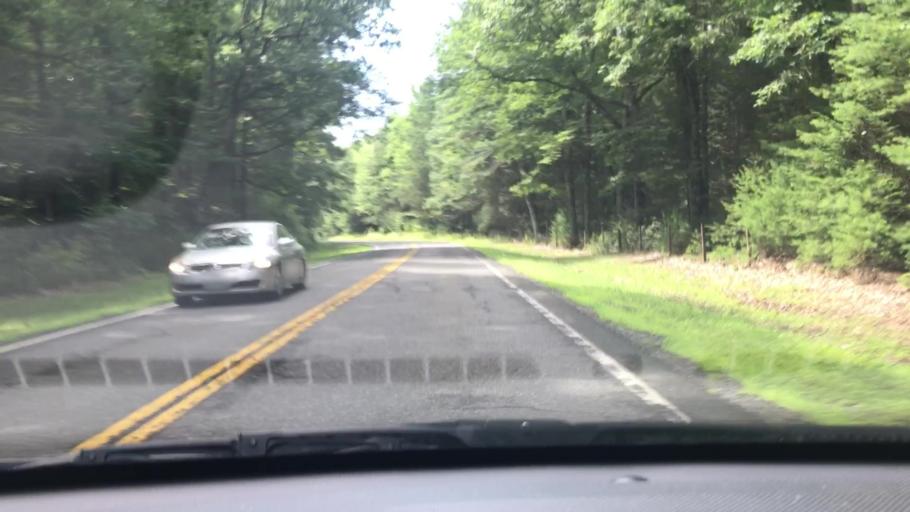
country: US
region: New York
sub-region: Ulster County
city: Shokan
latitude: 41.9615
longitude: -74.2068
